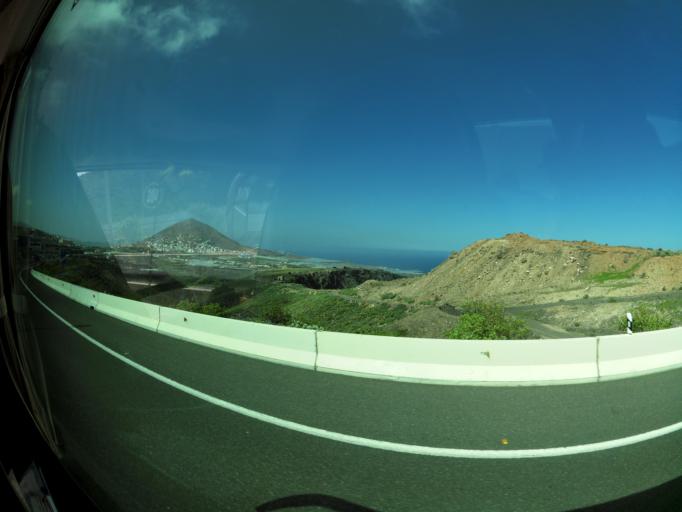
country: ES
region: Canary Islands
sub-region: Provincia de Las Palmas
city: Guia
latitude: 28.1447
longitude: -15.6116
